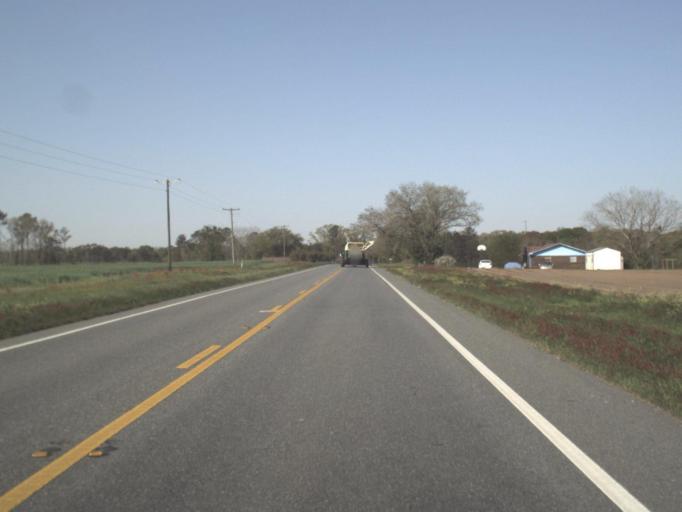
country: US
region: Florida
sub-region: Jackson County
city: Malone
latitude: 30.9498
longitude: -85.2474
